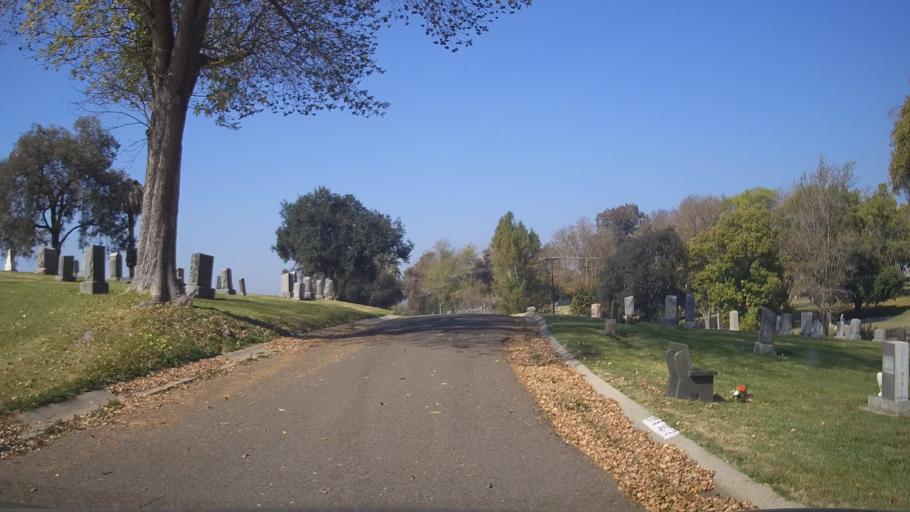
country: US
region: California
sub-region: San Diego County
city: National City
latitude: 32.7067
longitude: -117.1122
